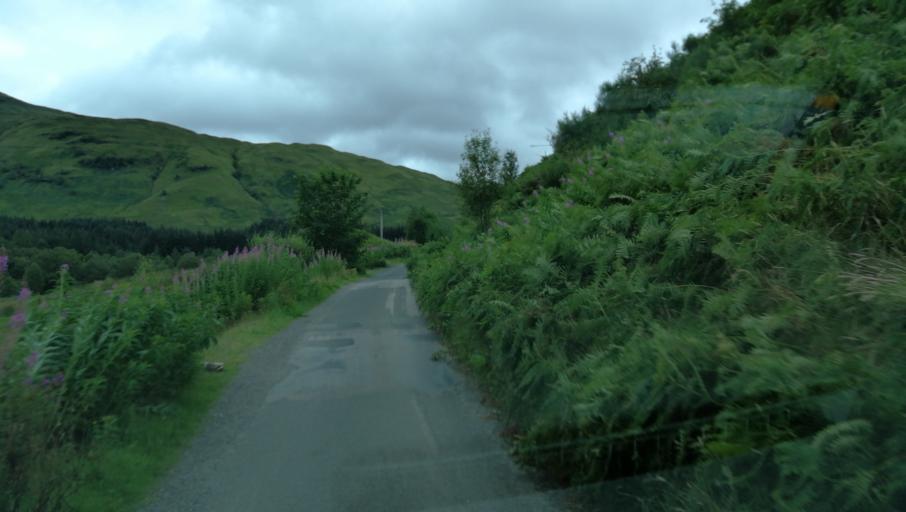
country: GB
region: Scotland
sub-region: Argyll and Bute
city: Garelochhead
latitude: 56.4238
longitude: -4.6734
